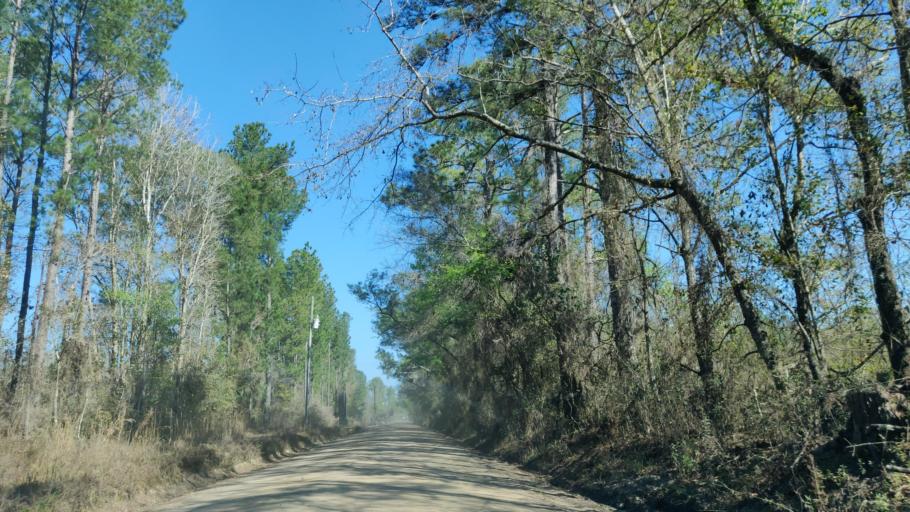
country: US
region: Florida
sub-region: Duval County
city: Baldwin
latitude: 30.1830
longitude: -81.9700
